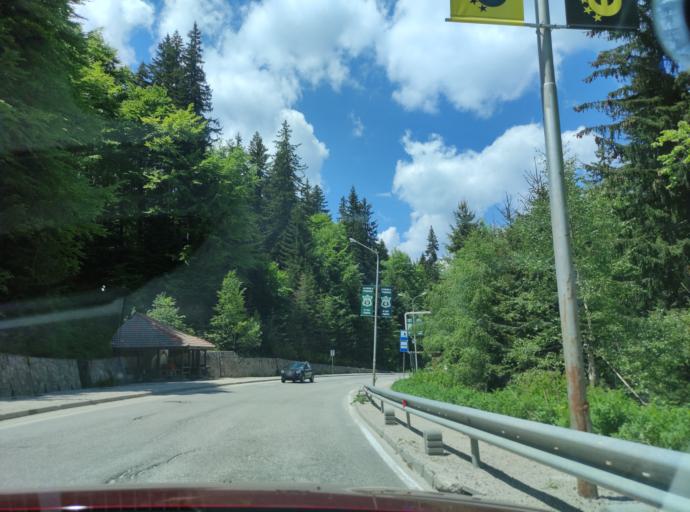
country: BG
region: Smolyan
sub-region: Obshtina Smolyan
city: Smolyan
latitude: 41.6394
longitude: 24.6940
